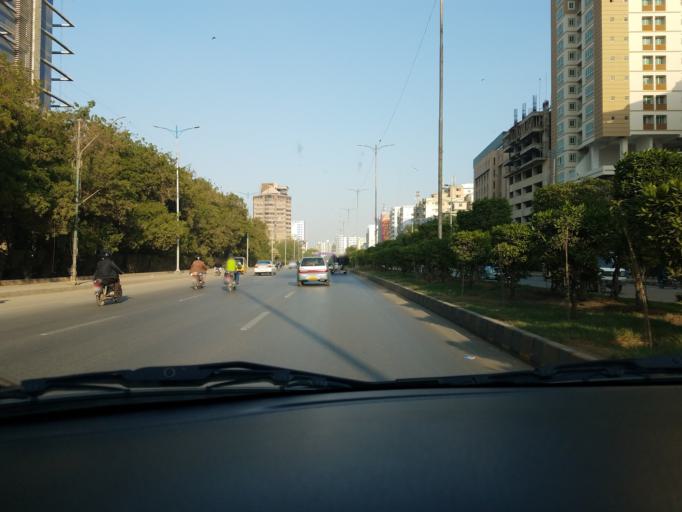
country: PK
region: Sindh
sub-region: Karachi District
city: Karachi
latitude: 24.8611
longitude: 67.0663
